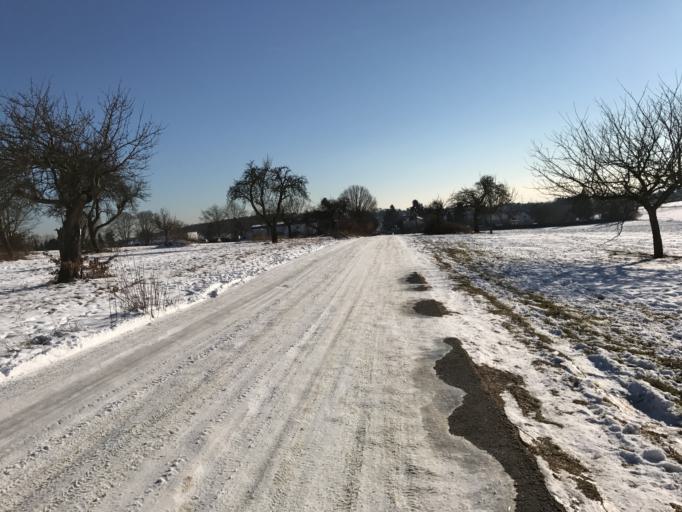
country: DE
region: Hesse
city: Eppstein
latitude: 50.1134
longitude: 8.3938
